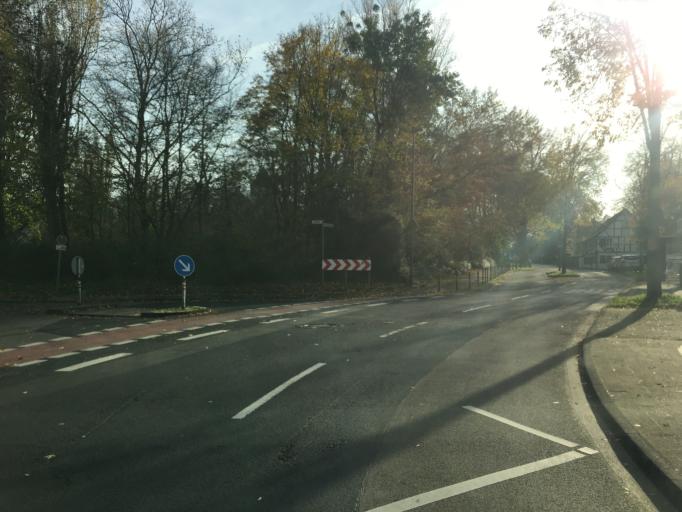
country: DE
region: North Rhine-Westphalia
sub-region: Regierungsbezirk Koln
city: Merheim
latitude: 50.9506
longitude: 7.0503
